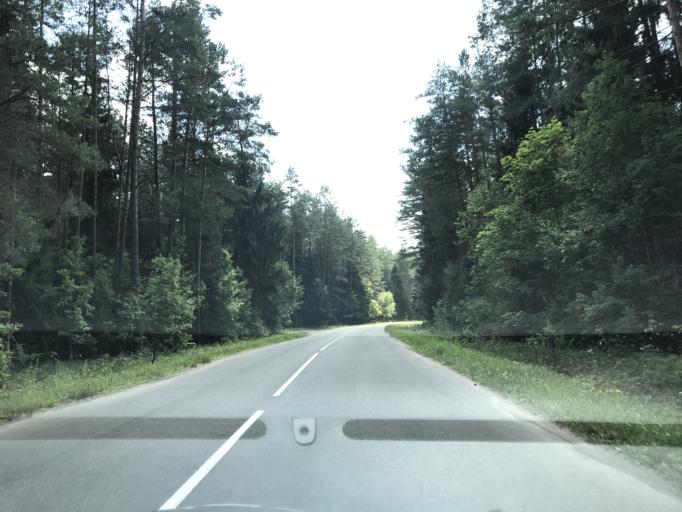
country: BY
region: Minsk
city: Rakaw
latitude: 53.9930
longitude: 26.9909
